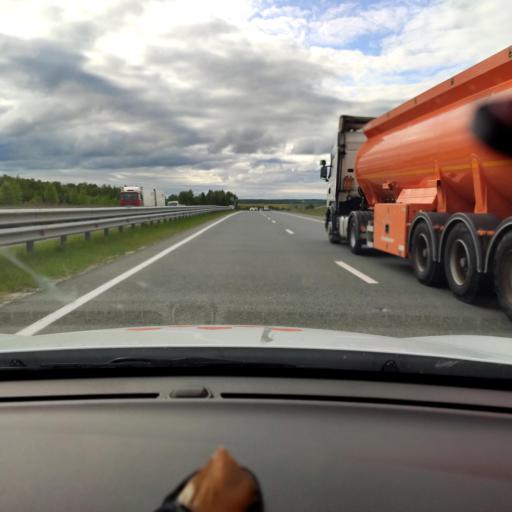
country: RU
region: Tatarstan
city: Pestretsy
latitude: 55.5496
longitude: 49.7427
